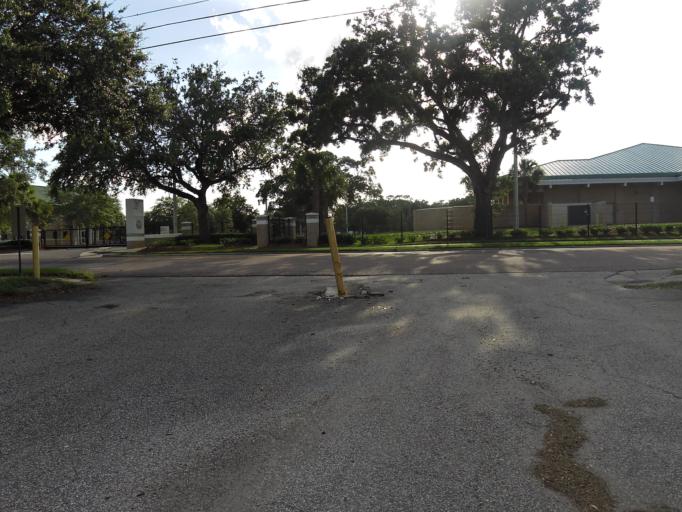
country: US
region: Florida
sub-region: Duval County
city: Jacksonville
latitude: 30.3363
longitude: -81.6639
